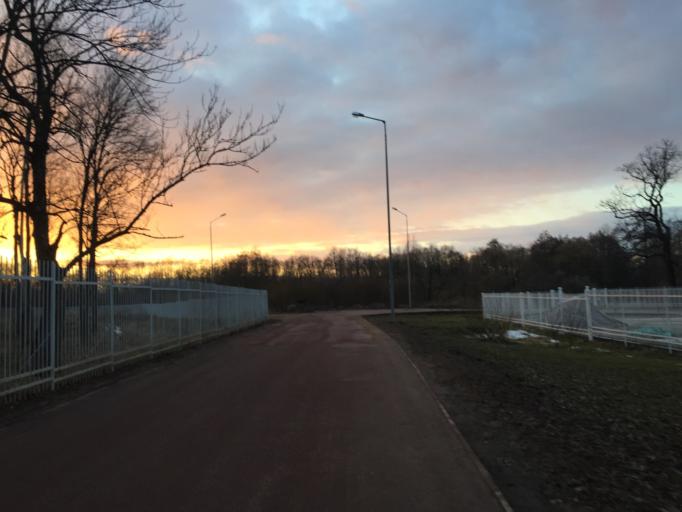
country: RU
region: St.-Petersburg
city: Pushkin
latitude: 59.7260
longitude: 30.3780
